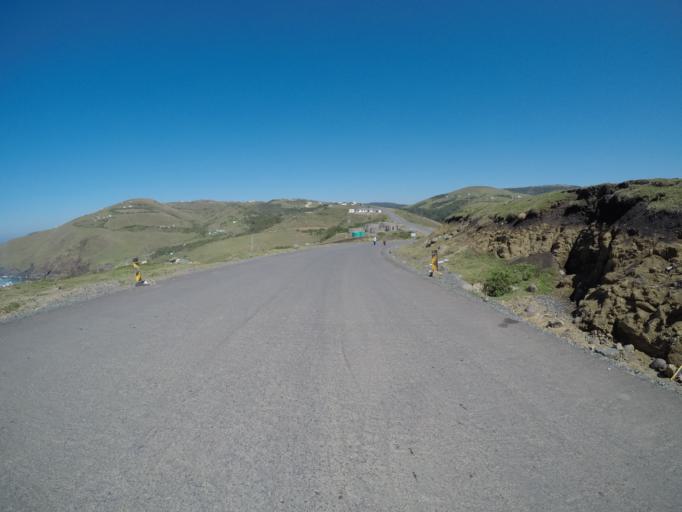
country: ZA
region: Eastern Cape
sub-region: OR Tambo District Municipality
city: Libode
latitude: -31.9925
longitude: 29.1397
